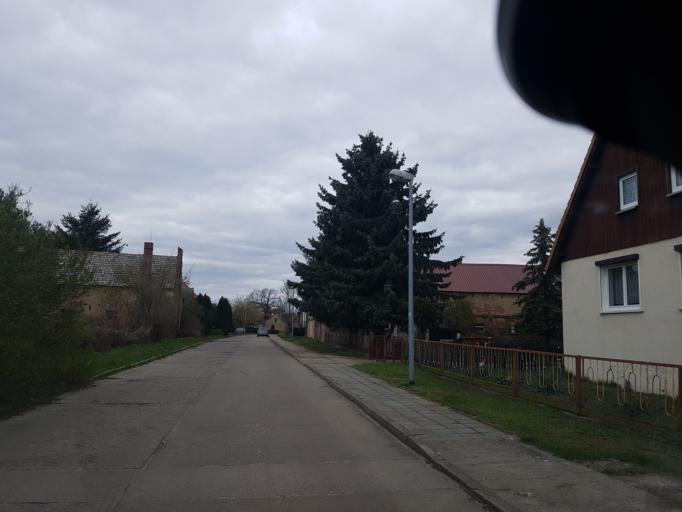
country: DE
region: Brandenburg
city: Borkheide
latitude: 52.1973
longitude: 12.8249
